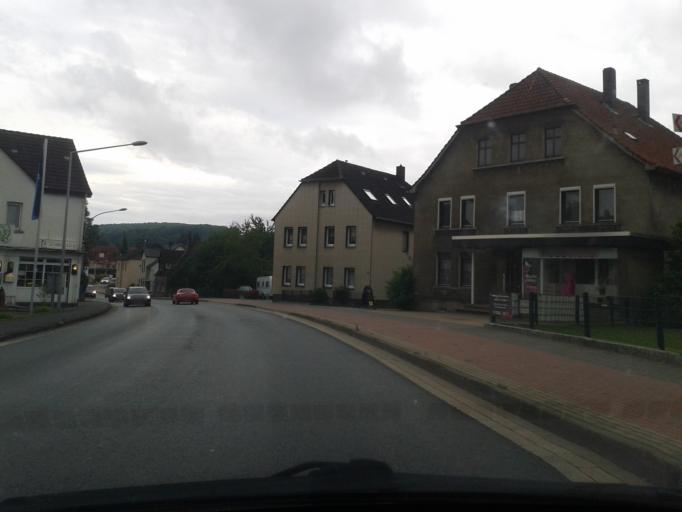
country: DE
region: North Rhine-Westphalia
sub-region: Regierungsbezirk Detmold
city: Detmold
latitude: 51.9213
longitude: 8.8998
